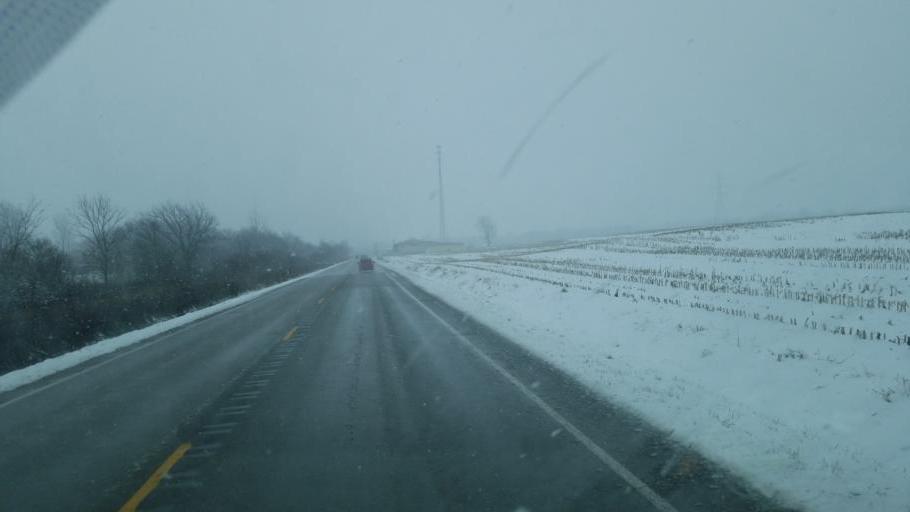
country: US
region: Indiana
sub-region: Wayne County
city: Hagerstown
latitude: 40.0286
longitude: -85.1961
